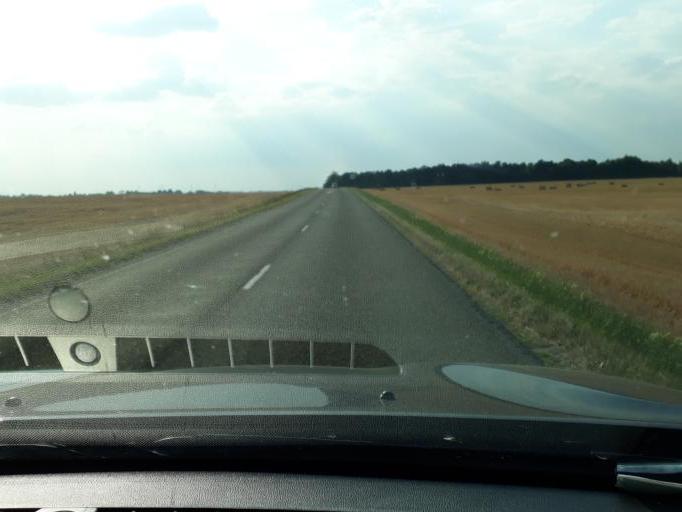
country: FR
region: Centre
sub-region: Departement du Loir-et-Cher
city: Ouzouer-le-Marche
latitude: 47.8654
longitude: 1.5911
